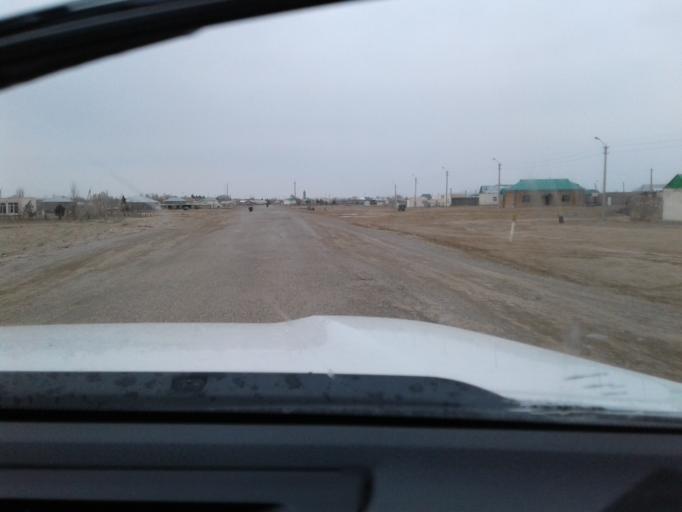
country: TM
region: Ahal
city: Abadan
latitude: 38.7560
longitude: 58.4907
